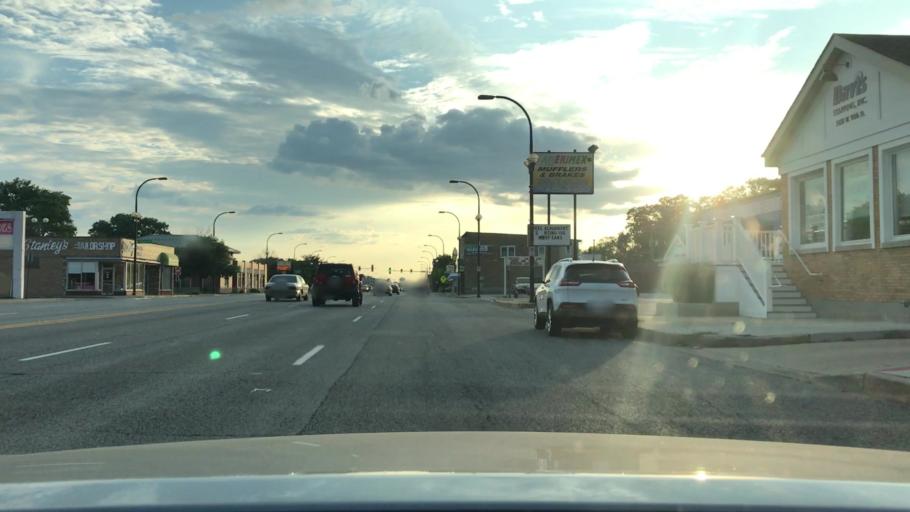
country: US
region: Illinois
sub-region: Cook County
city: Oak Lawn
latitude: 41.7199
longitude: -87.7572
